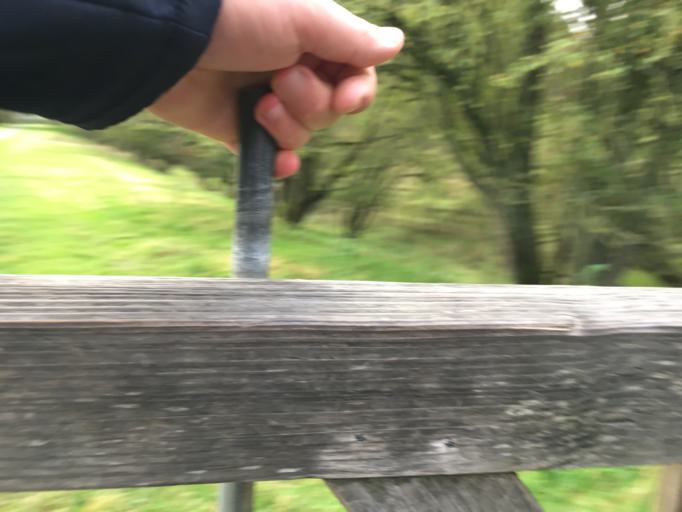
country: GB
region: England
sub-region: North Yorkshire
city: Sleights
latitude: 54.4033
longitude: -0.7218
